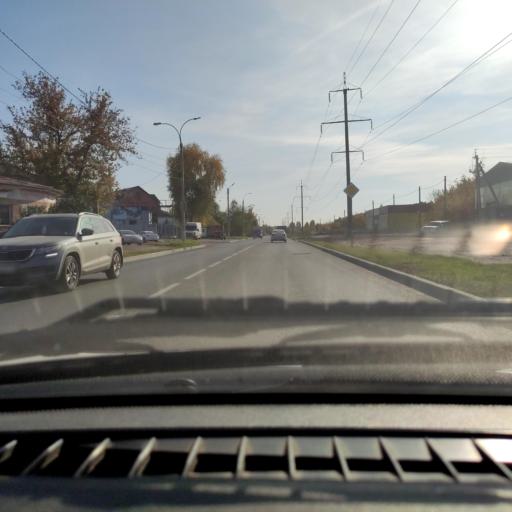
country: RU
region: Samara
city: Tol'yatti
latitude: 53.5226
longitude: 49.3958
